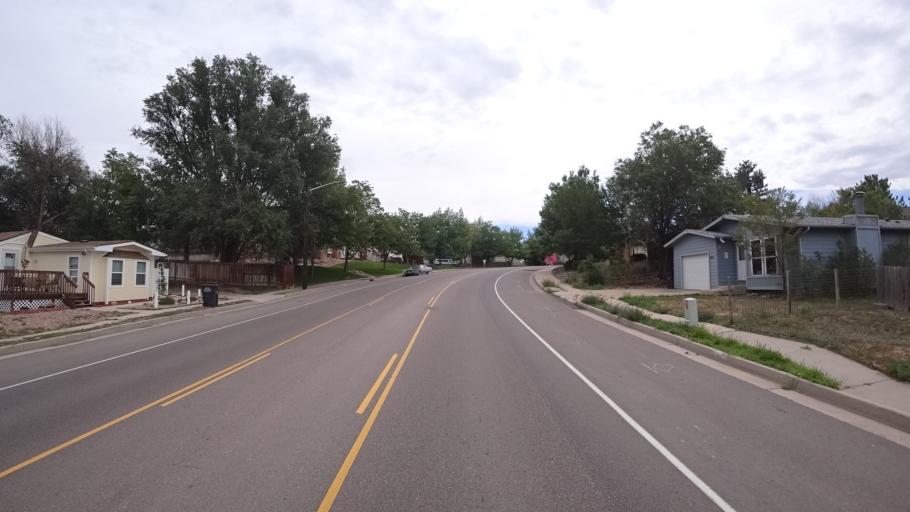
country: US
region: Colorado
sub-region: El Paso County
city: Fountain
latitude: 38.6972
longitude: -104.7007
